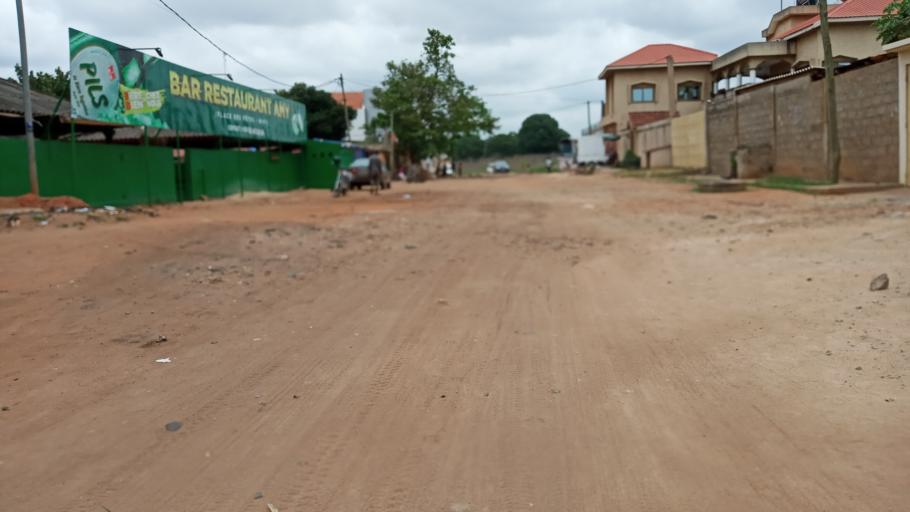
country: TG
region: Maritime
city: Lome
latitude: 6.1848
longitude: 1.1680
